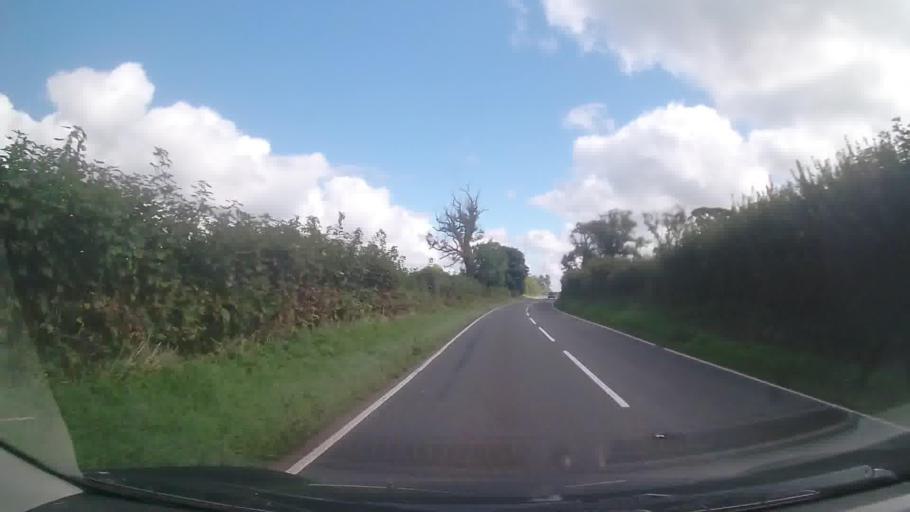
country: GB
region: Wales
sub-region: Pembrokeshire
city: Pembroke
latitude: 51.6879
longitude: -4.8708
